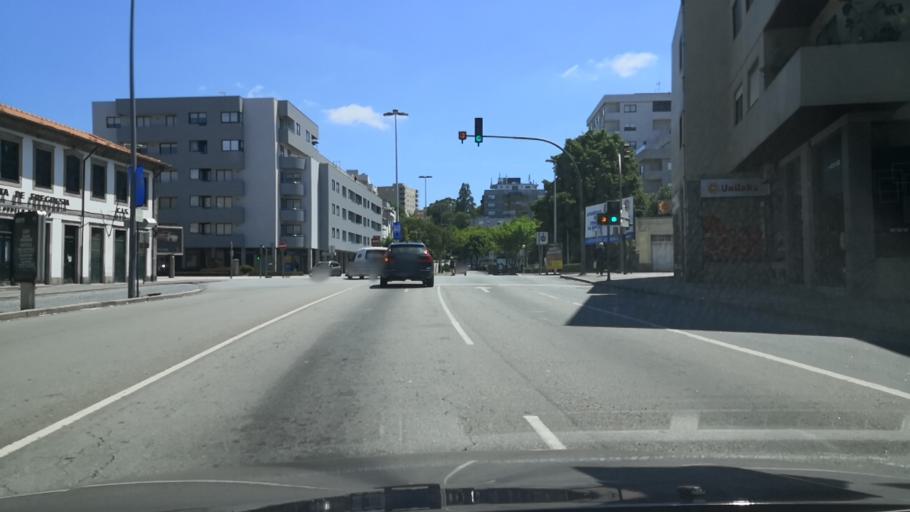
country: PT
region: Porto
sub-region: Vila Nova de Gaia
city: Canidelo
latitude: 41.1541
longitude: -8.6489
